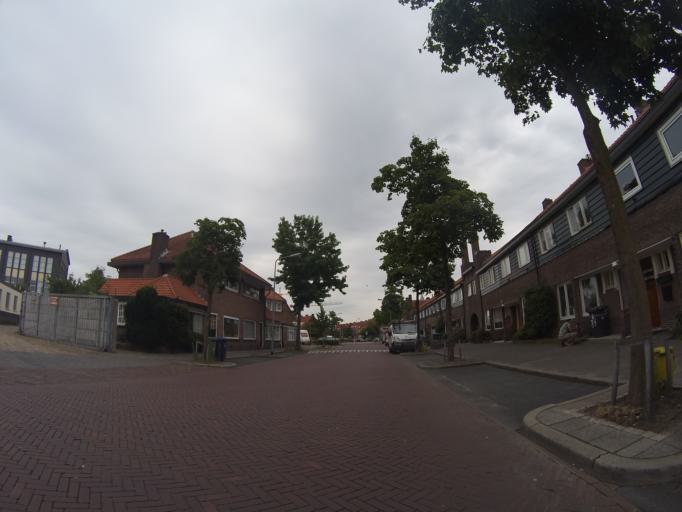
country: NL
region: North Holland
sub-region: Gemeente Hilversum
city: Hilversum
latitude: 52.2261
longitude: 5.1865
